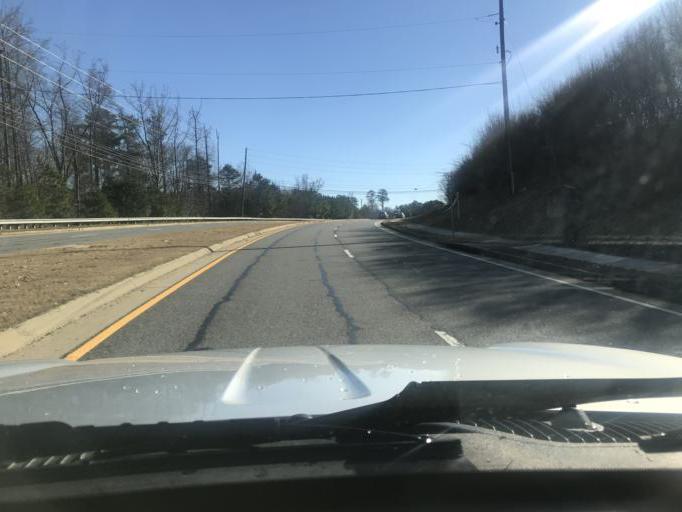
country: US
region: Georgia
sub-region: Gwinnett County
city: Lawrenceville
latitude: 33.9748
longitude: -84.0608
